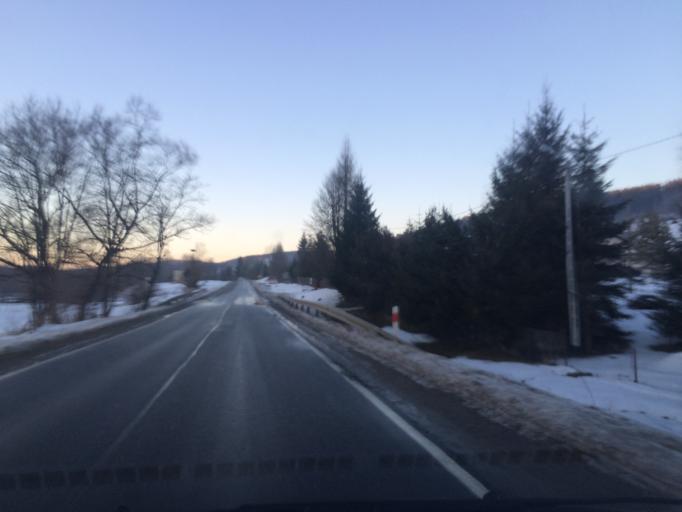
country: PL
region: Subcarpathian Voivodeship
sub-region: Powiat bieszczadzki
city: Czarna
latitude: 49.3744
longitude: 22.6460
